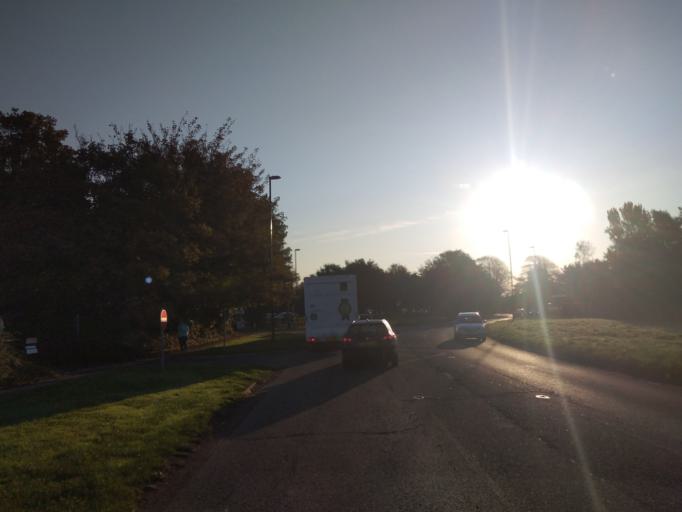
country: GB
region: England
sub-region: West Sussex
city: Rustington
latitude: 50.8185
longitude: -0.4706
